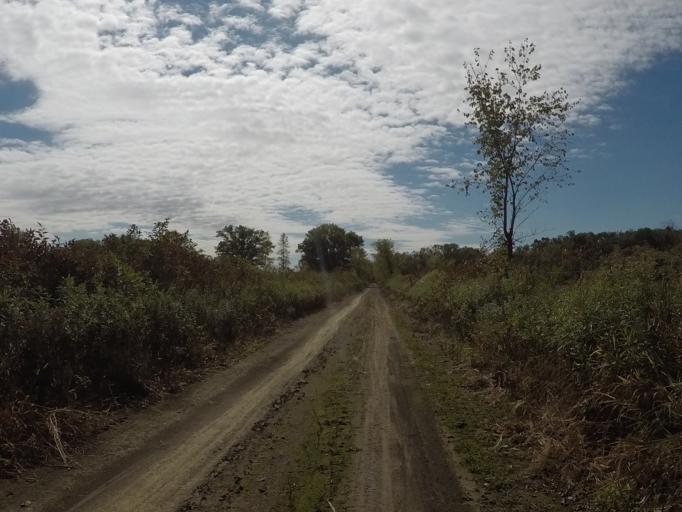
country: US
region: Wisconsin
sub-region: Richland County
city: Richland Center
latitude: 43.2434
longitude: -90.3045
